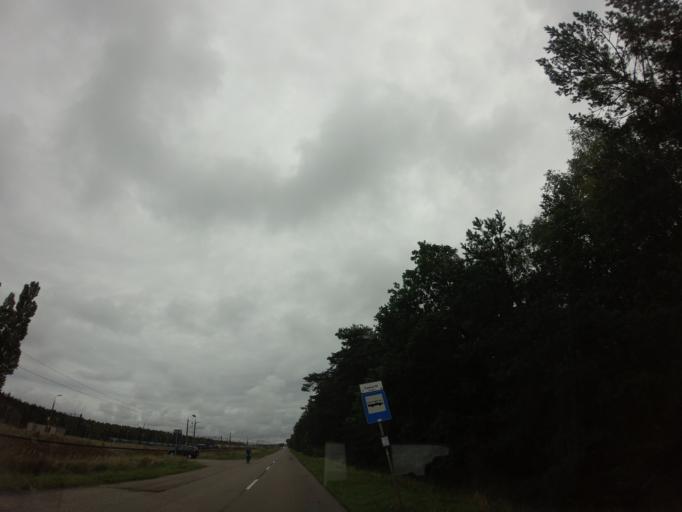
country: PL
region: West Pomeranian Voivodeship
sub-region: Swinoujscie
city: Swinoujscie
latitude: 53.8984
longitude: 14.3154
